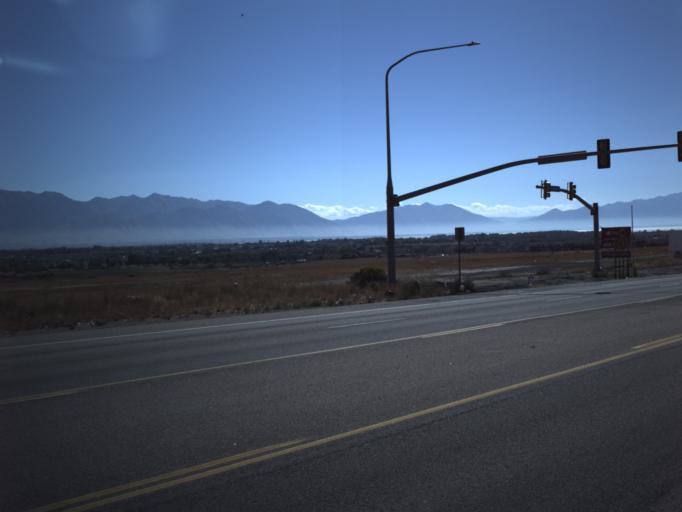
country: US
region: Utah
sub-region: Utah County
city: Saratoga Springs
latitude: 40.4000
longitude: -111.9195
